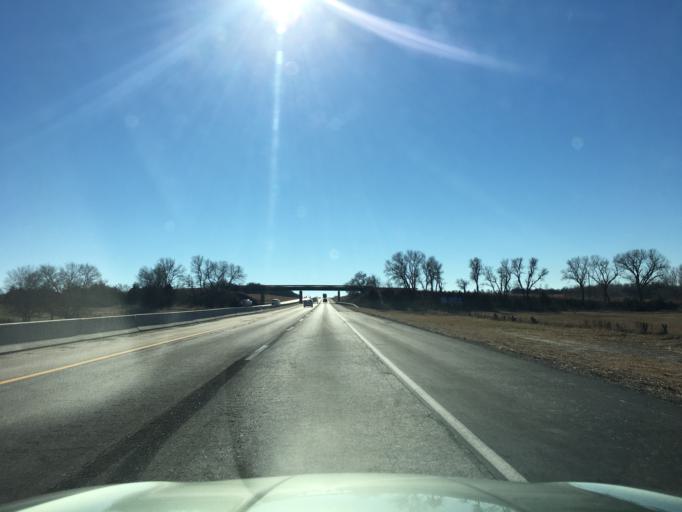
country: US
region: Kansas
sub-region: Sumner County
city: Wellington
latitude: 37.0886
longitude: -97.3387
